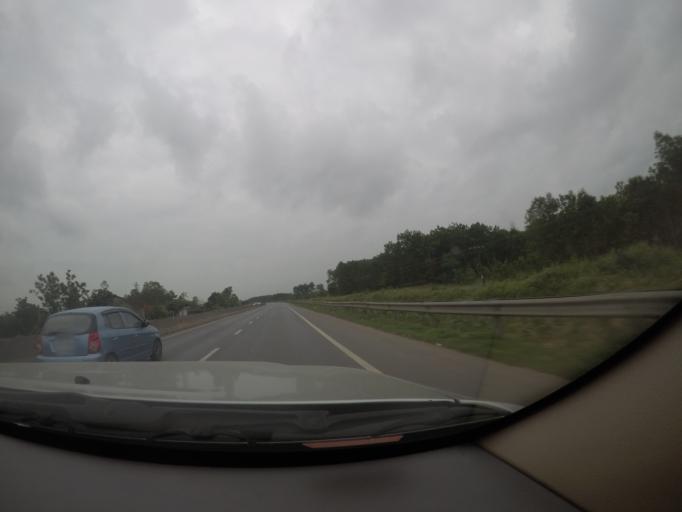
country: VN
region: Quang Tri
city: Hai Lang
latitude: 16.6989
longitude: 107.2290
